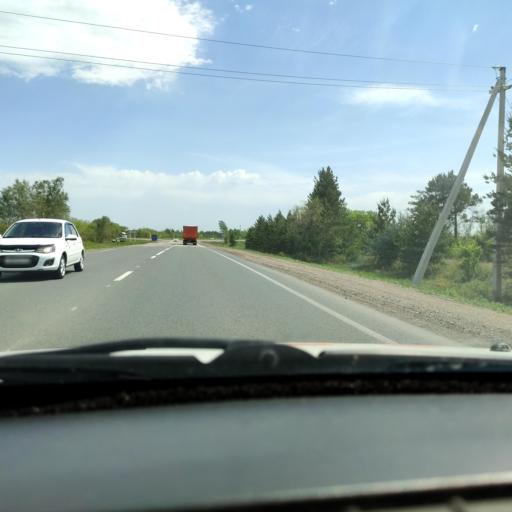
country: RU
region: Samara
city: Mirnyy
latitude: 53.5257
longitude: 50.3142
